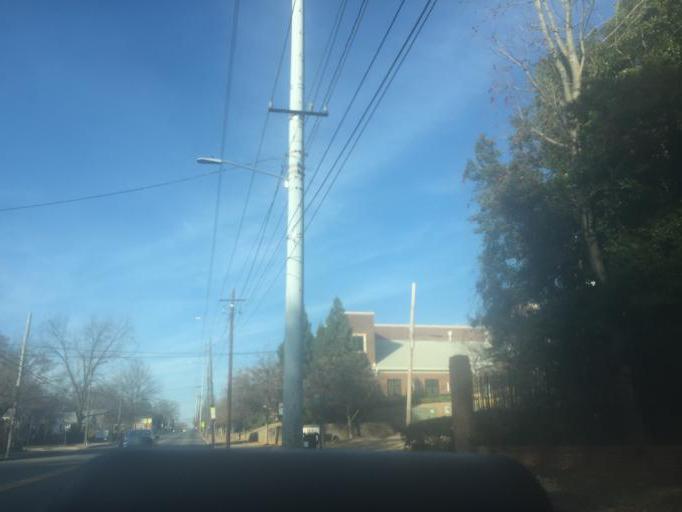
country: US
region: Georgia
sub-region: Fulton County
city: Atlanta
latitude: 33.7278
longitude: -84.4079
